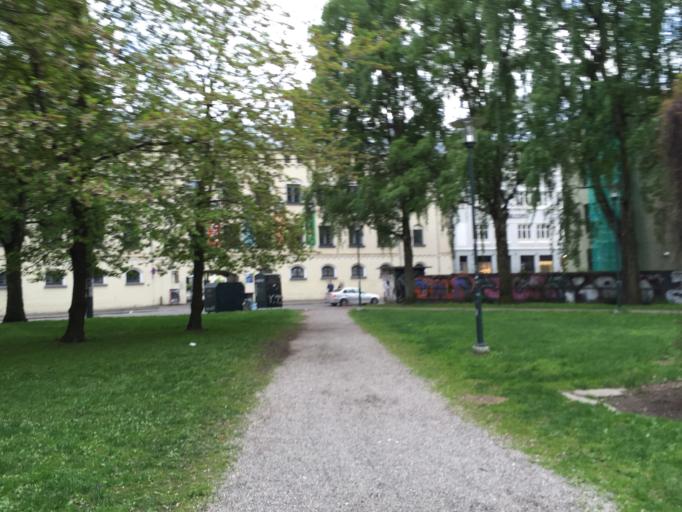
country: NO
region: Oslo
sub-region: Oslo
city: Oslo
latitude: 59.9205
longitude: 10.7605
